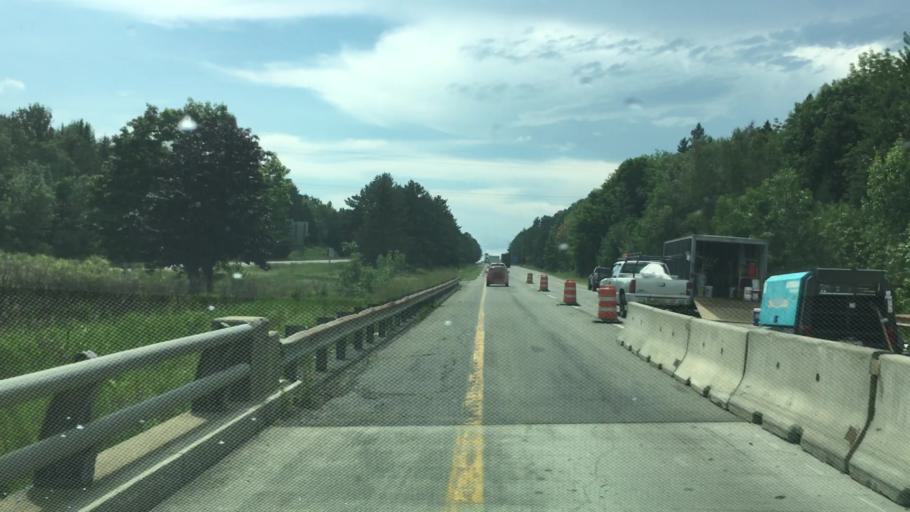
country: US
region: Maine
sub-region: Penobscot County
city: Medway
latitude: 45.6008
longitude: -68.5309
